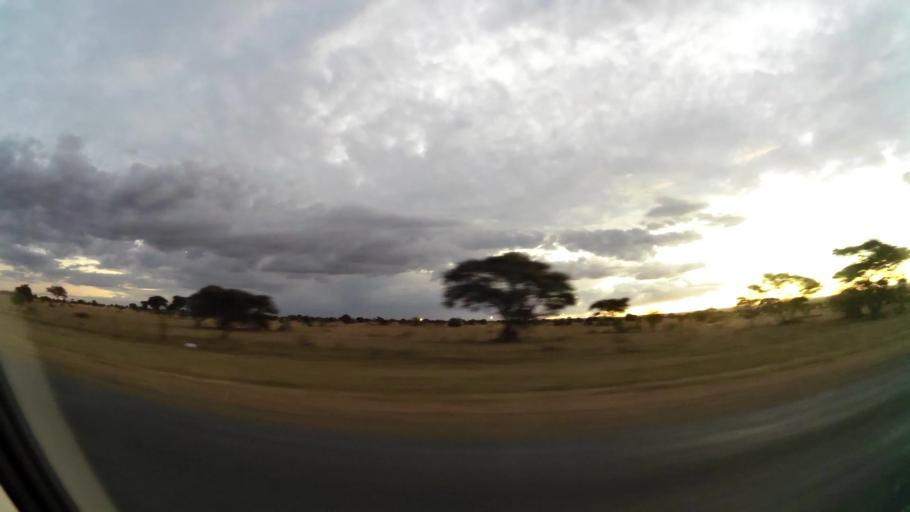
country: ZA
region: Limpopo
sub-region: Capricorn District Municipality
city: Polokwane
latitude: -23.8345
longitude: 29.4265
